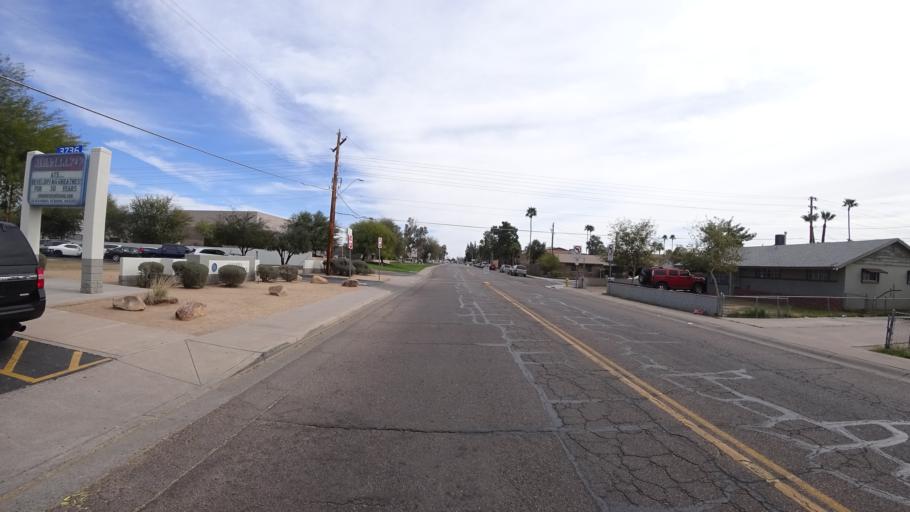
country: US
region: Arizona
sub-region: Maricopa County
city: Glendale
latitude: 33.4877
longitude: -112.1391
